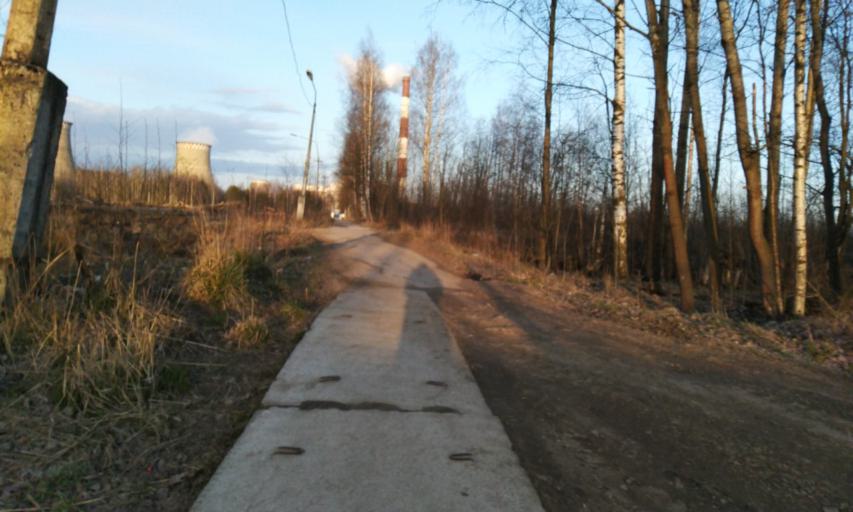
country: RU
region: Leningrad
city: Novoye Devyatkino
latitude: 60.0768
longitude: 30.4606
